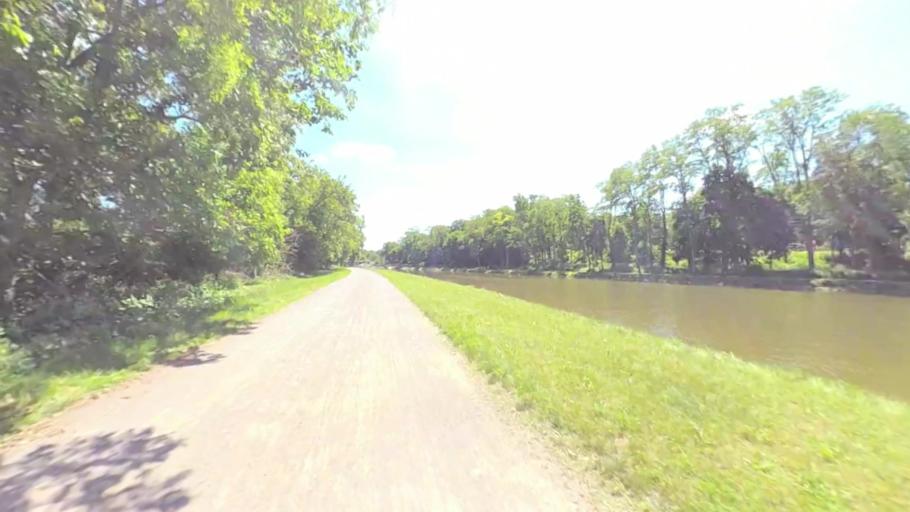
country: US
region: New York
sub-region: Monroe County
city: Pittsford
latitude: 43.0632
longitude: -77.4817
